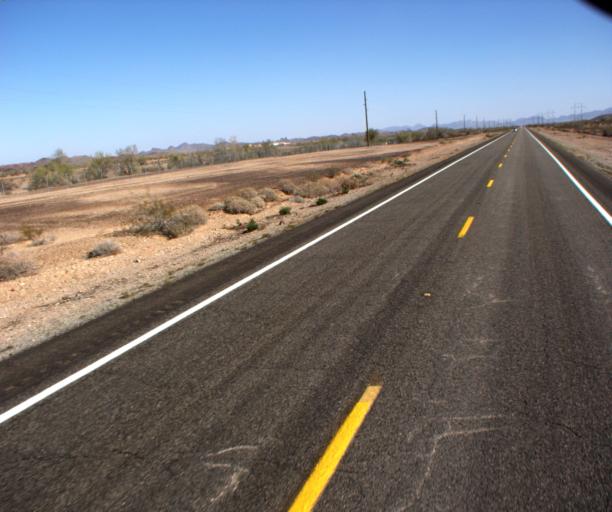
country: US
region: Arizona
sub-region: Yuma County
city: Fortuna Foothills
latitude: 32.9032
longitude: -114.3316
